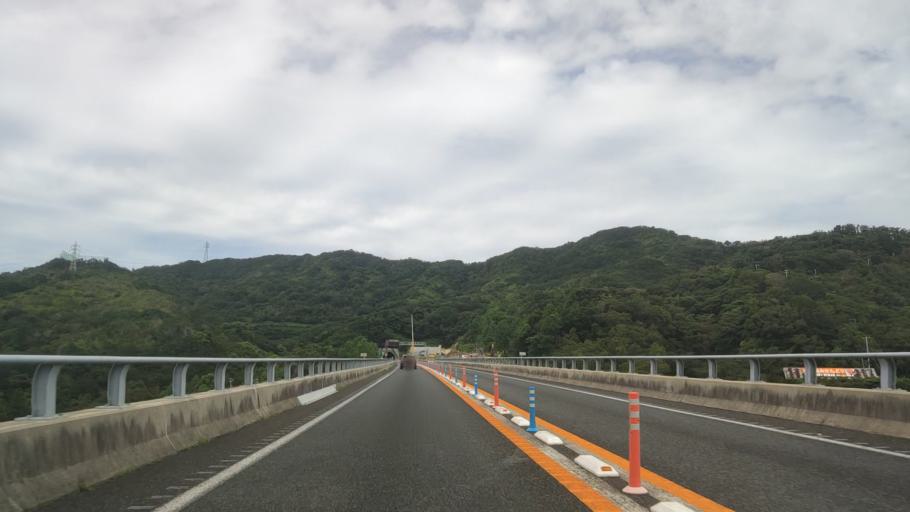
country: JP
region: Wakayama
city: Gobo
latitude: 33.8452
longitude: 135.2184
